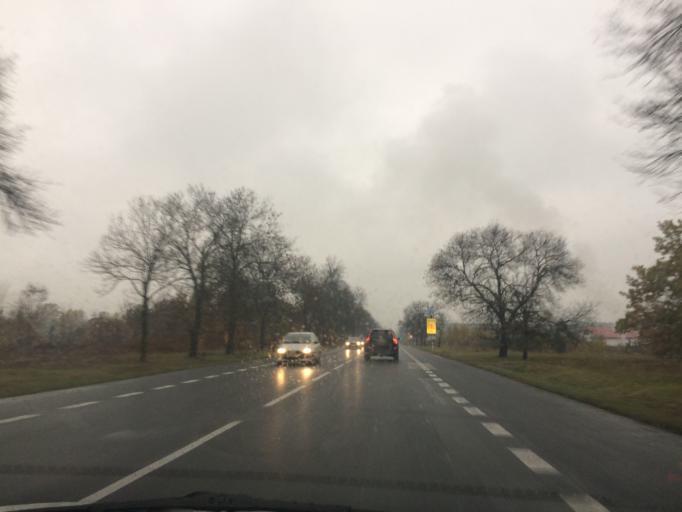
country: PL
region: Masovian Voivodeship
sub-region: Powiat otwocki
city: Otwock
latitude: 52.1346
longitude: 21.3384
